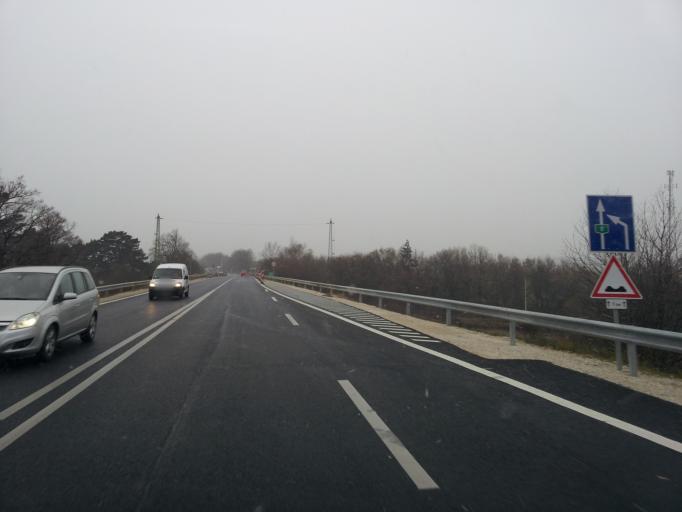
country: HU
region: Veszprem
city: Herend
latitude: 47.1388
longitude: 17.7248
